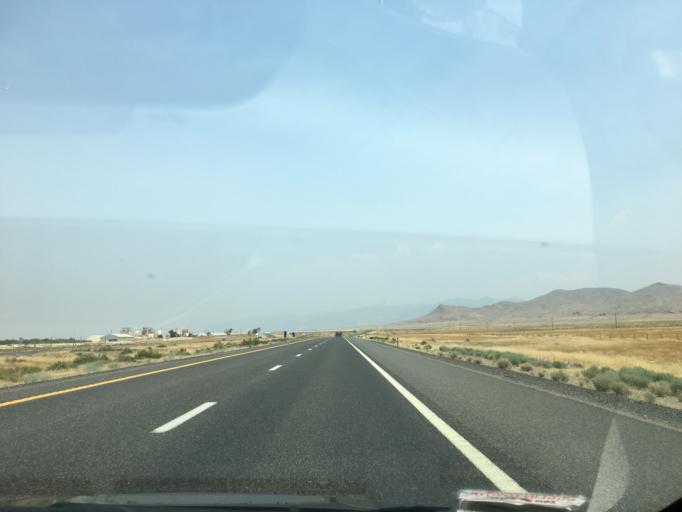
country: US
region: Nevada
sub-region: Pershing County
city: Lovelock
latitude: 40.2357
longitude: -118.3949
